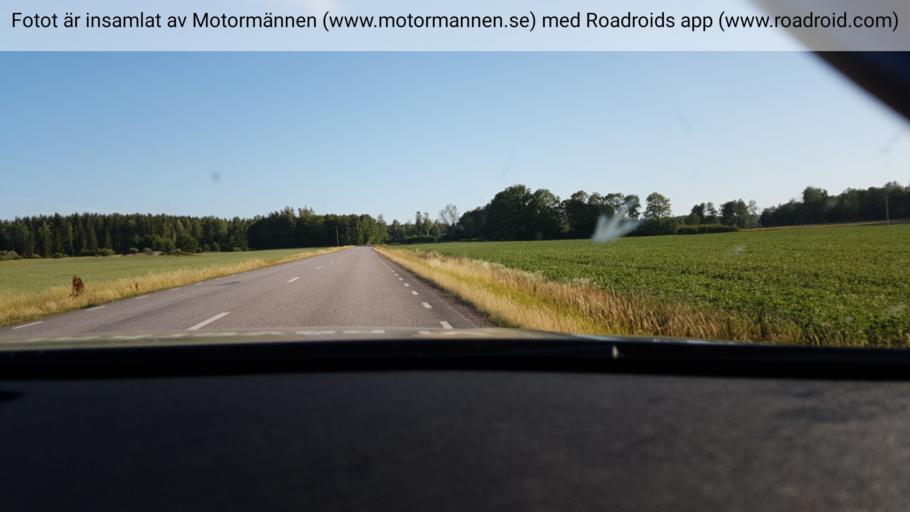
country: SE
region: Vaestra Goetaland
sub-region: Skovde Kommun
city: Stopen
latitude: 58.5308
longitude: 13.9929
